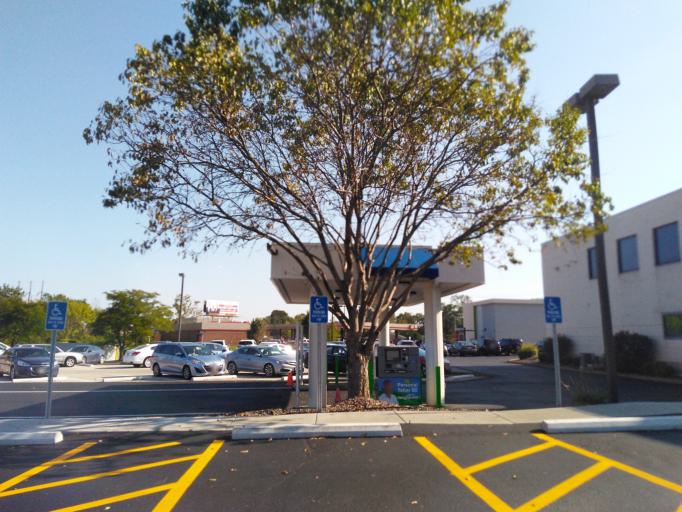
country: US
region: Missouri
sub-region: Saint Louis County
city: Green Park
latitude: 38.5159
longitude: -90.3420
